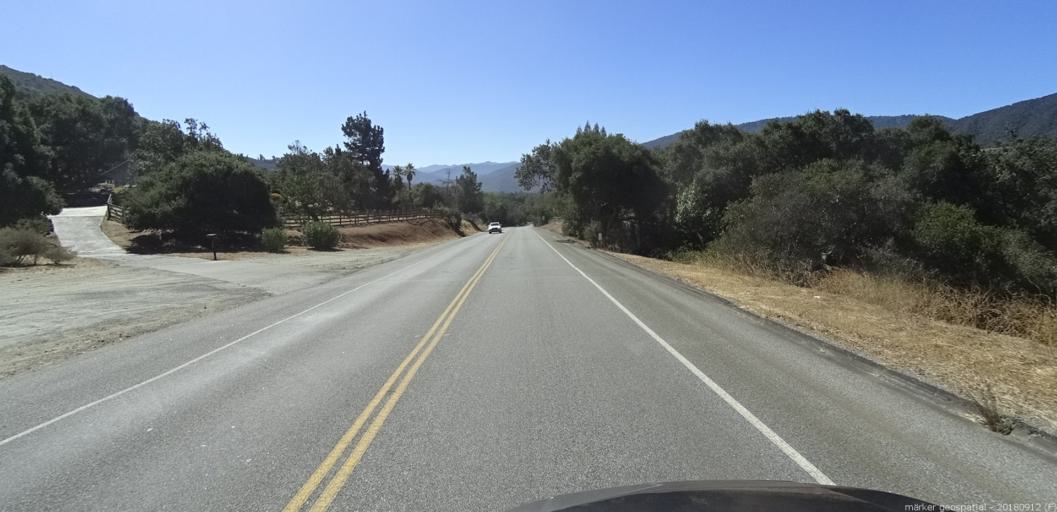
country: US
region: California
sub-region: Monterey County
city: Carmel Valley Village
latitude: 36.5106
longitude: -121.7545
